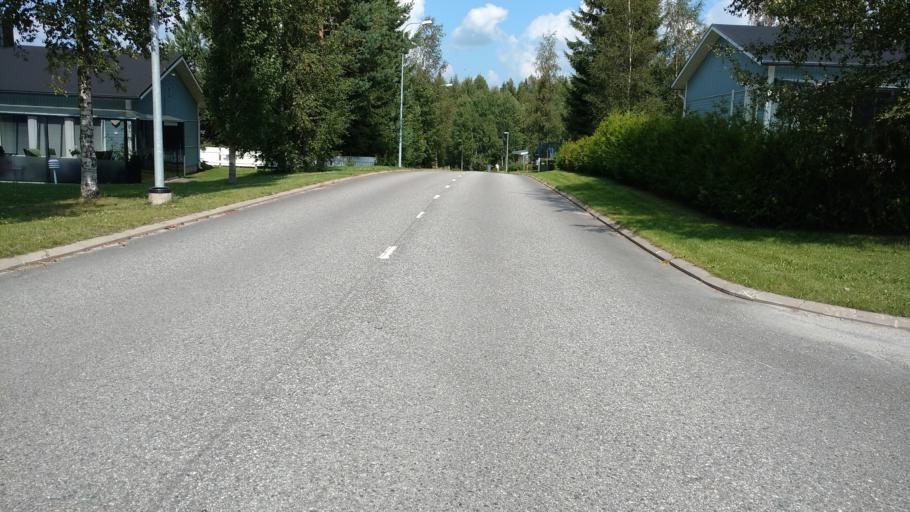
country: FI
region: Varsinais-Suomi
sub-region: Salo
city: Salo
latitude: 60.4067
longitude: 23.1952
